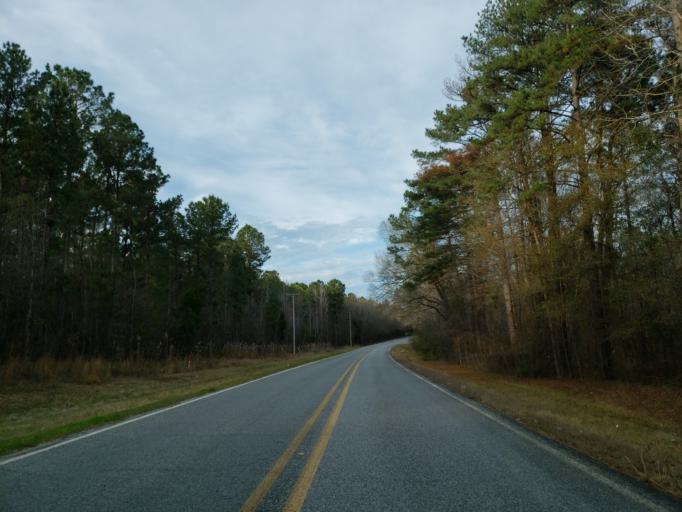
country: US
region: Mississippi
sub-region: Wayne County
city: Waynesboro
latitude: 31.8375
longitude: -88.6894
